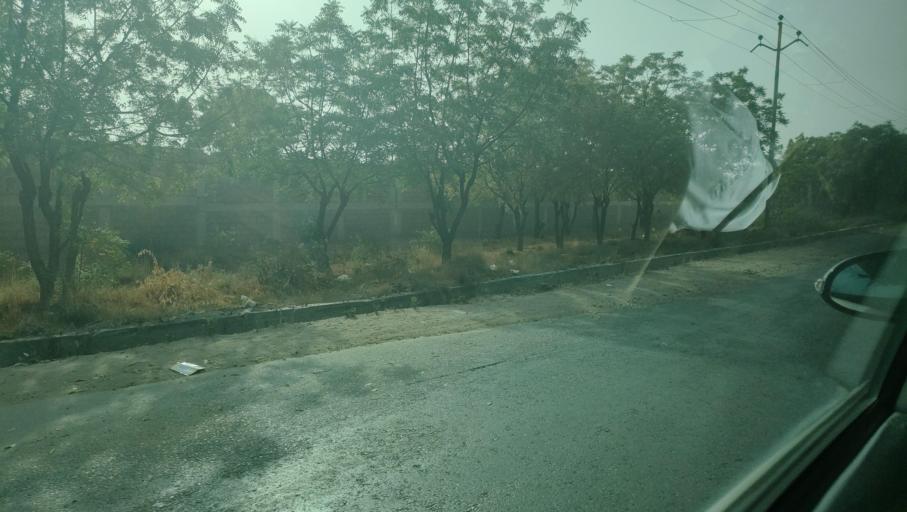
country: PK
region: Sindh
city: Malir Cantonment
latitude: 24.9262
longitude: 67.1800
